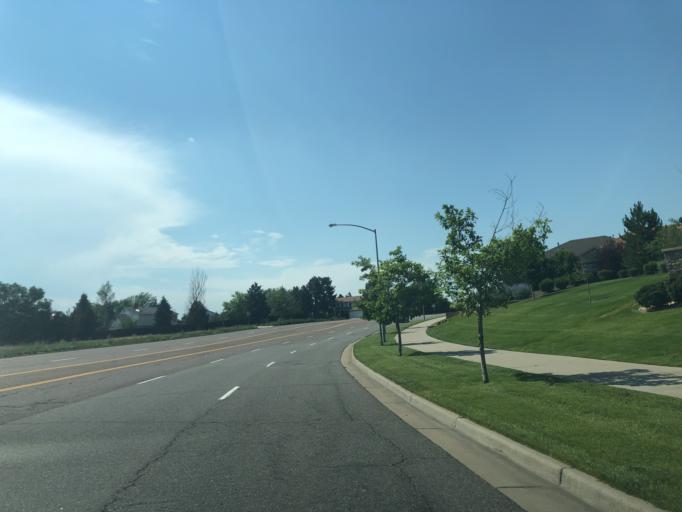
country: US
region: Colorado
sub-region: Arapahoe County
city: Dove Valley
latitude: 39.6351
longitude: -104.7621
